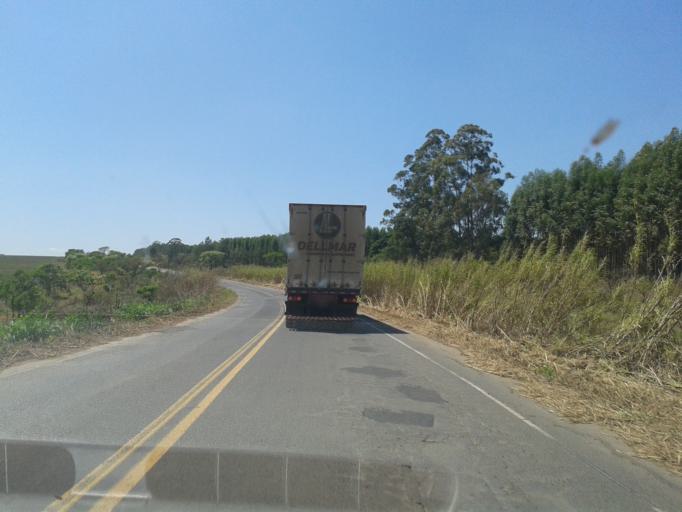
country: BR
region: Minas Gerais
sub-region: Araxa
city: Araxa
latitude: -19.4364
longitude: -47.2110
